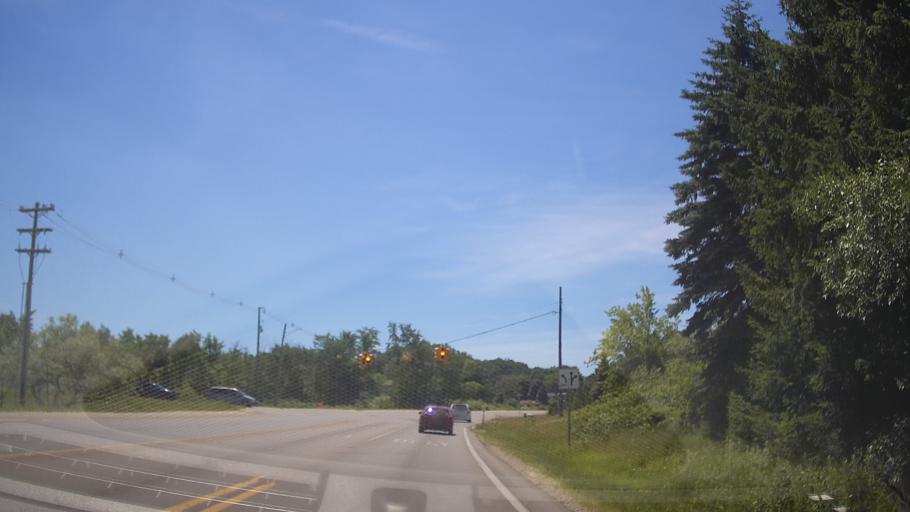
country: US
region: Michigan
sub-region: Grand Traverse County
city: Traverse City
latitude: 44.7291
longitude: -85.6635
